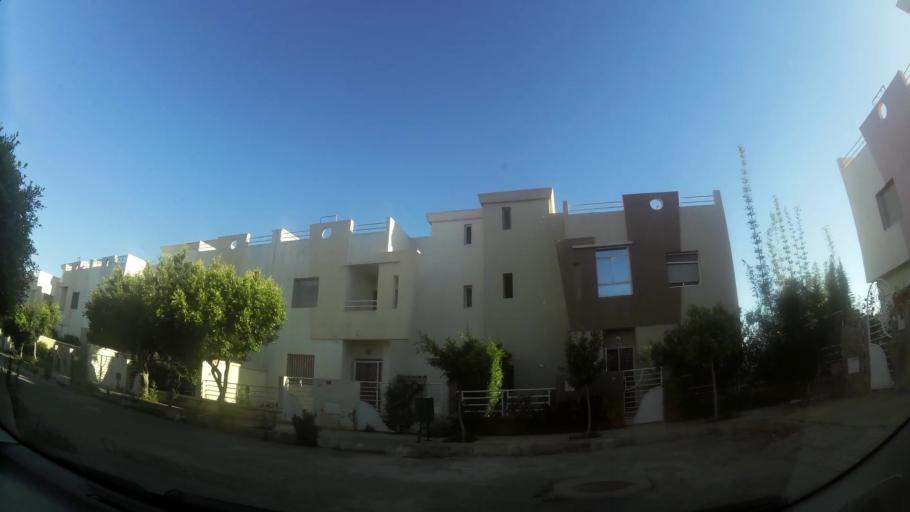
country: MA
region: Oriental
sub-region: Berkane-Taourirt
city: Madagh
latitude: 35.0846
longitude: -2.2502
